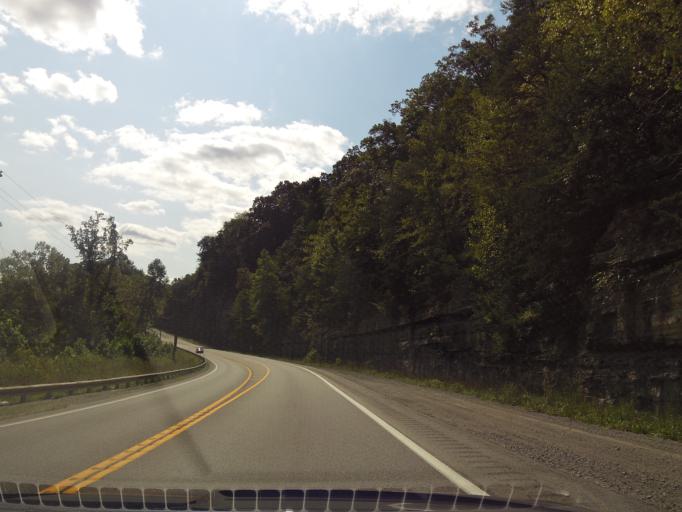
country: US
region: Kentucky
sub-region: Harlan County
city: Loyall
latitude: 36.8360
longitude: -83.4173
